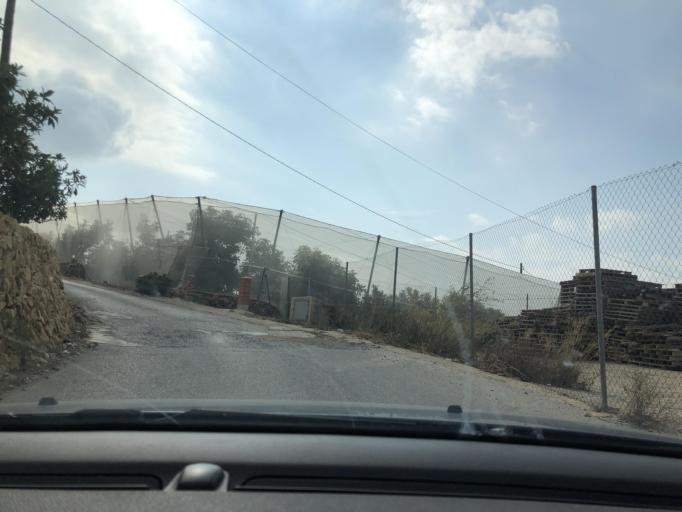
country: ES
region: Valencia
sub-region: Provincia de Alicante
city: Callosa d'En Sarria
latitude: 38.6371
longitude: -0.1175
